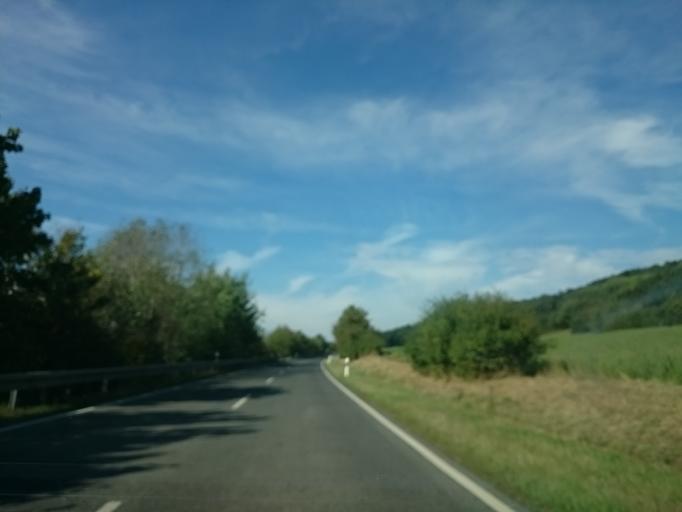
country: DE
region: Bavaria
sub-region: Regierungsbezirk Mittelfranken
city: Heideck
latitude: 49.1319
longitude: 11.1103
